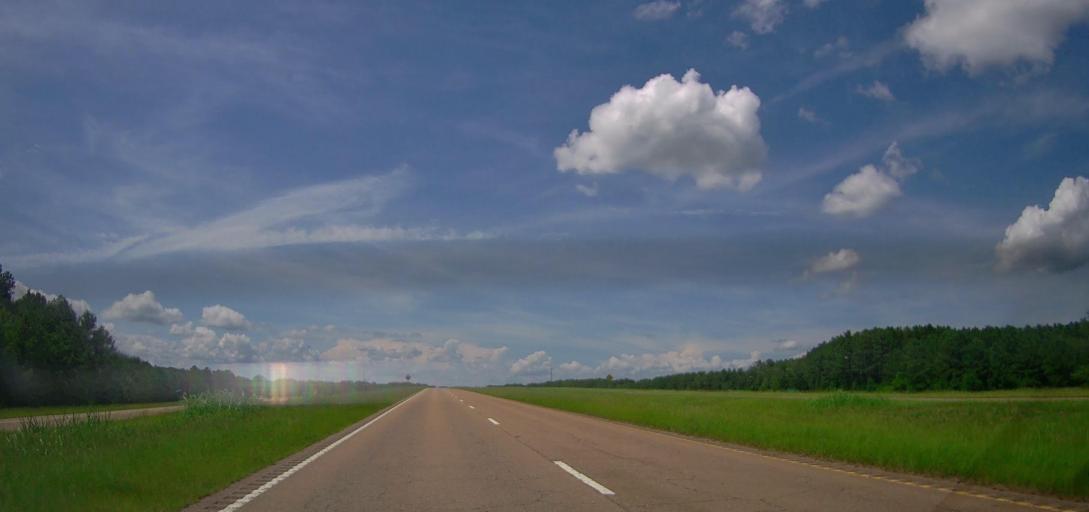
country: US
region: Mississippi
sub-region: Monroe County
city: Aberdeen
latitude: 33.8366
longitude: -88.5902
